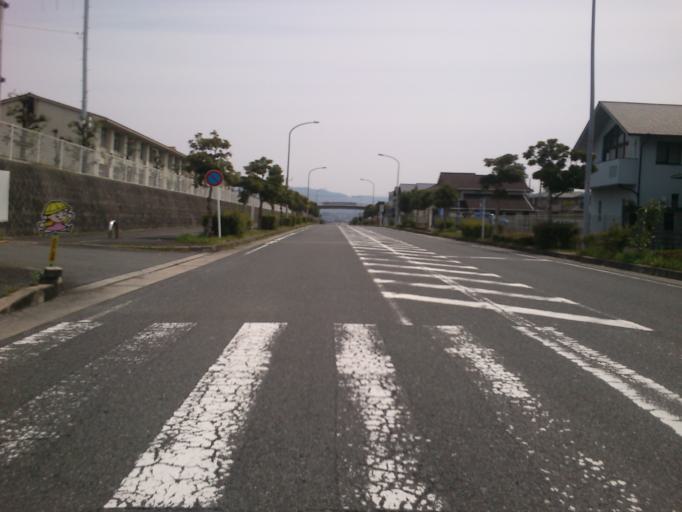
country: JP
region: Nara
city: Nara-shi
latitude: 34.7271
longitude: 135.7953
